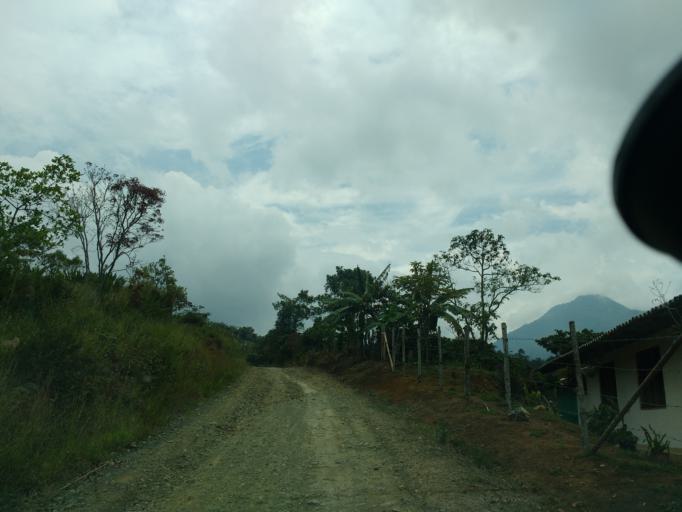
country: CO
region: Cauca
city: Santander de Quilichao
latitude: 2.9137
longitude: -76.4805
